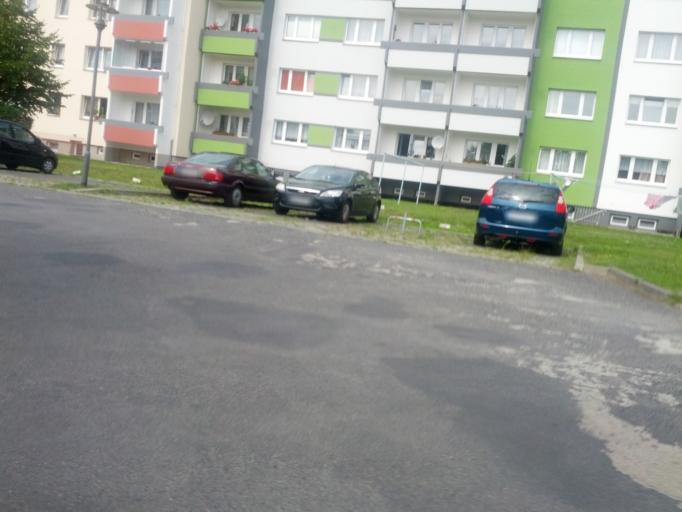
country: DE
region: Mecklenburg-Vorpommern
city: Bastorf
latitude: 54.1495
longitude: 11.7225
